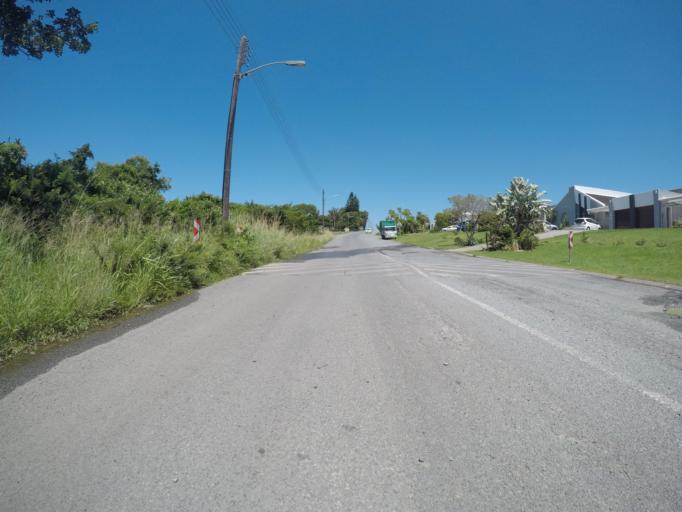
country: ZA
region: Eastern Cape
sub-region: Buffalo City Metropolitan Municipality
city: East London
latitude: -32.9638
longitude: 27.9544
